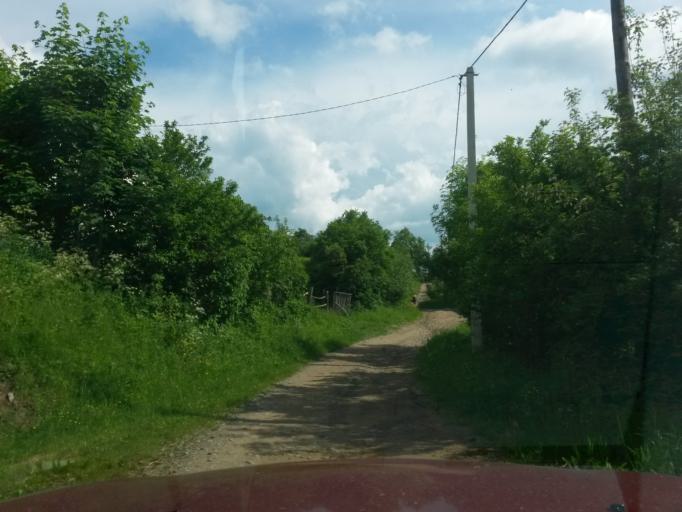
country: UA
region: Zakarpattia
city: Velykyi Bereznyi
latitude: 48.9007
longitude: 22.5271
